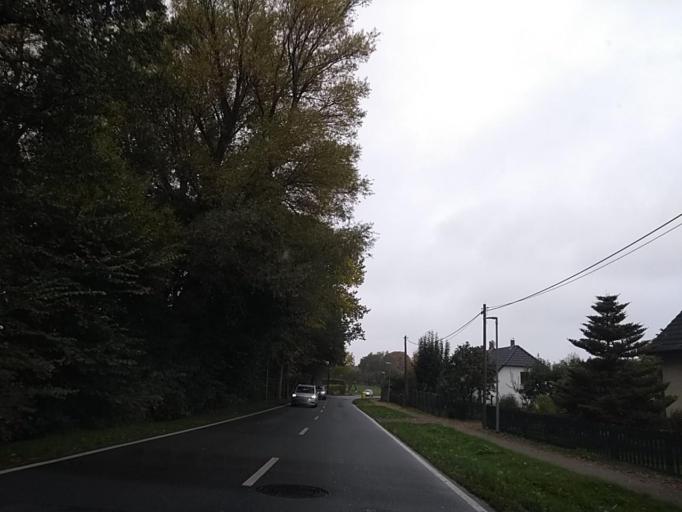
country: DE
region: Mecklenburg-Vorpommern
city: Ostseebad Kuhlungsborn
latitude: 54.1268
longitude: 11.7548
